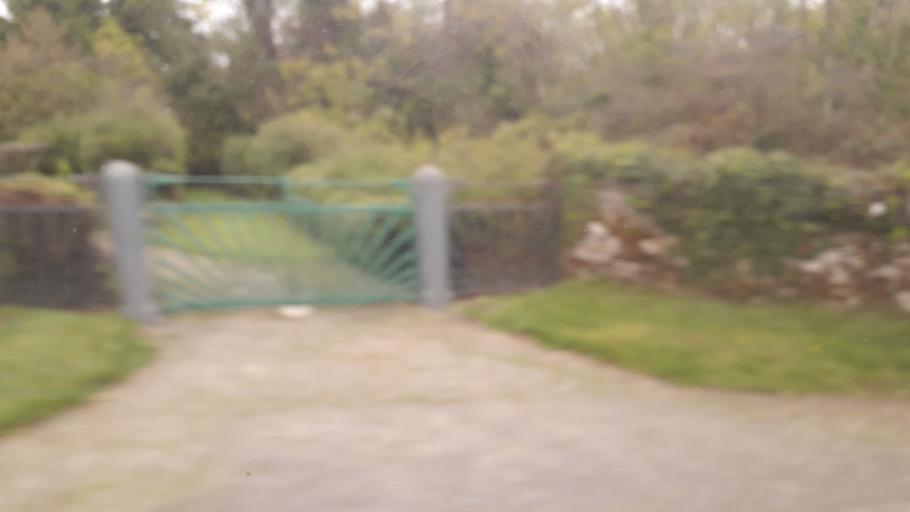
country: IE
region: Leinster
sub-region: Uibh Fhaili
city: Birr
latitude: 52.9762
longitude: -7.9518
